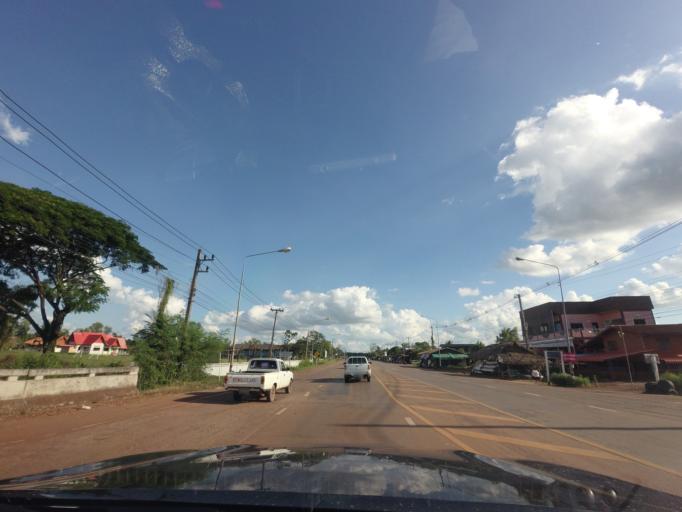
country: TH
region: Changwat Udon Thani
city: Ban Dung
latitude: 17.7095
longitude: 103.2505
